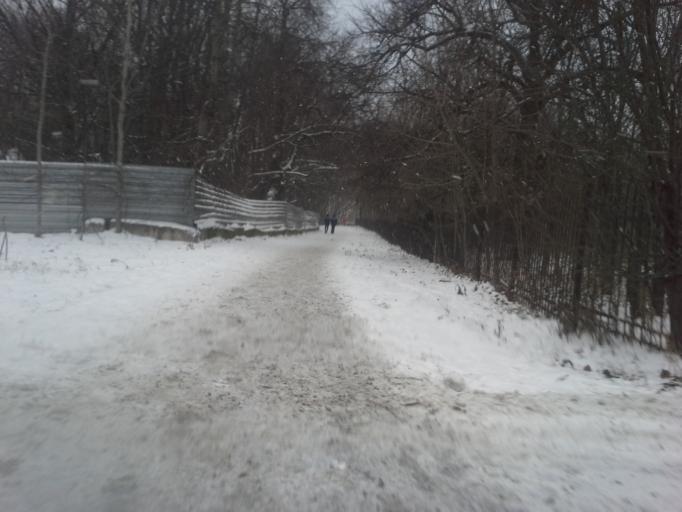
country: RU
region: Moscow
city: Yasenevo
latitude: 55.5987
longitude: 37.5492
